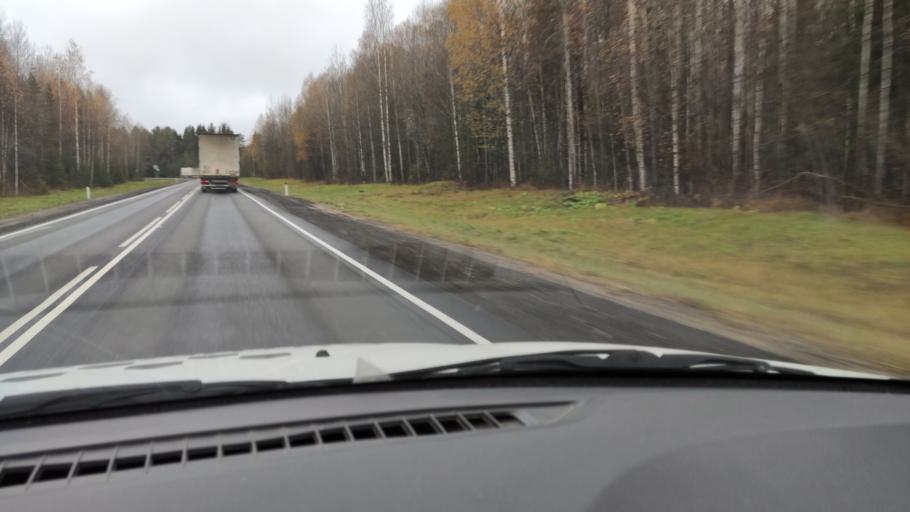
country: RU
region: Kirov
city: Belaya Kholunitsa
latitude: 58.8291
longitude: 50.6367
